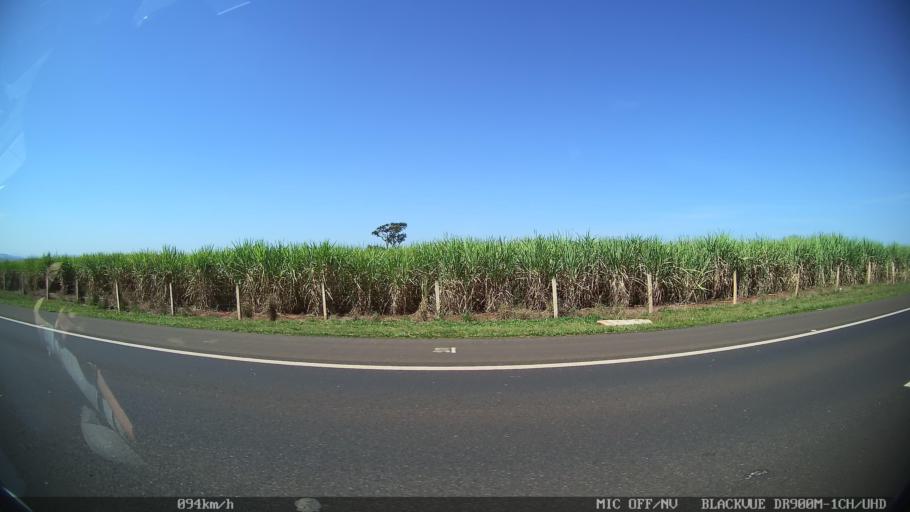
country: BR
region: Sao Paulo
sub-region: Batatais
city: Batatais
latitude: -20.7753
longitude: -47.5449
